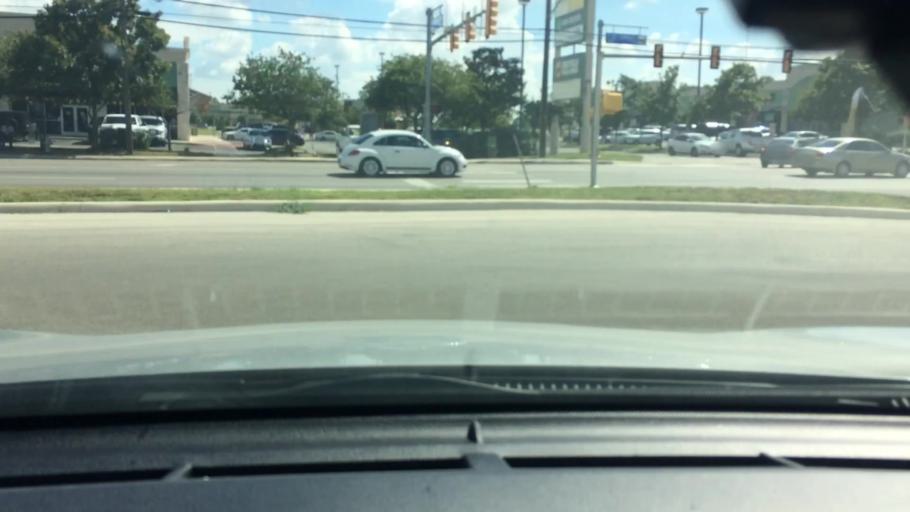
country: US
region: Texas
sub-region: Bexar County
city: Shavano Park
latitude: 29.5634
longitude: -98.5994
